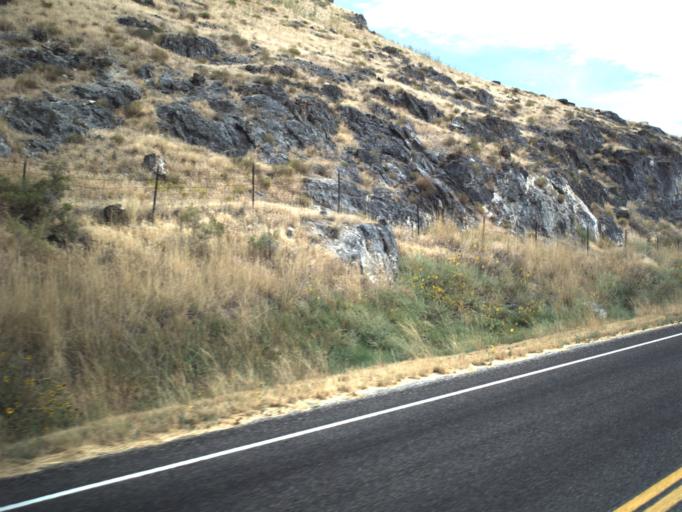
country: US
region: Utah
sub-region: Box Elder County
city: Elwood
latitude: 41.5803
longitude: -112.2540
